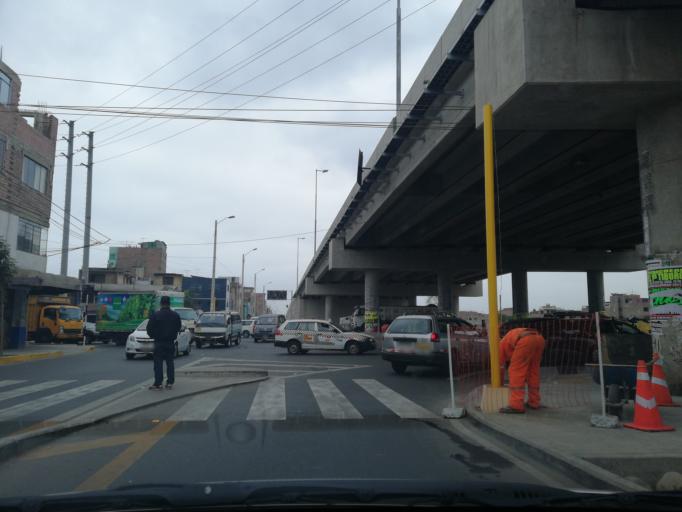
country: PE
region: Lima
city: Lima
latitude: -12.0355
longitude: -77.0654
